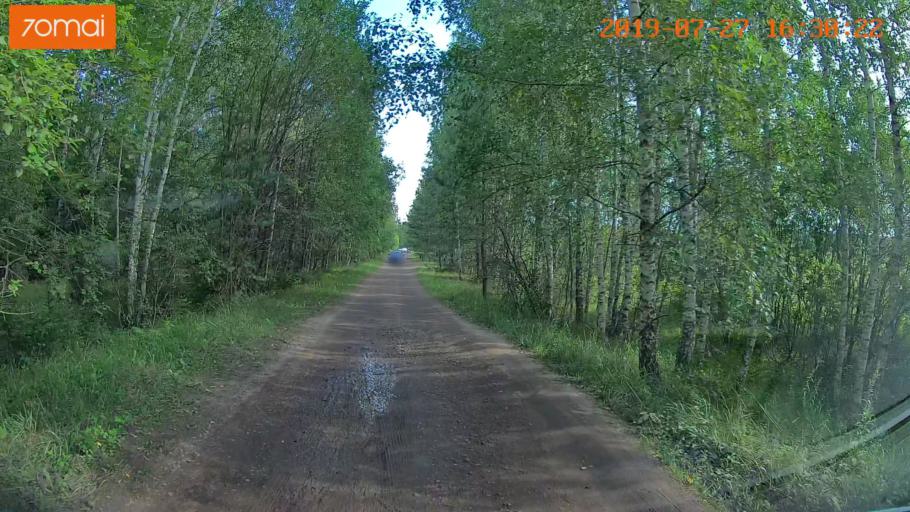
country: RU
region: Ivanovo
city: Novo-Talitsy
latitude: 57.0924
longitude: 40.8520
